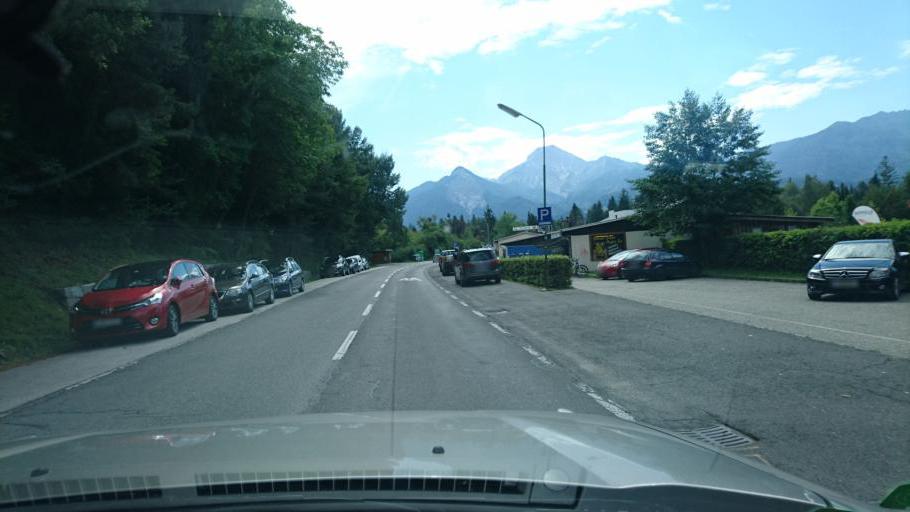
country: AT
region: Carinthia
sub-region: Politischer Bezirk Villach Land
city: Wernberg
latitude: 46.5807
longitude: 13.9353
